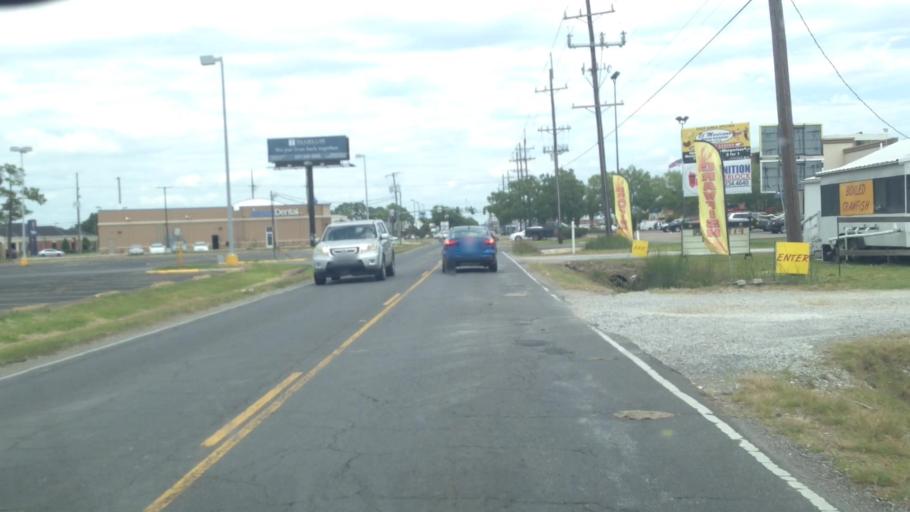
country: US
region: Louisiana
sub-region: Iberia Parish
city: New Iberia
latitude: 29.9844
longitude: -91.8226
